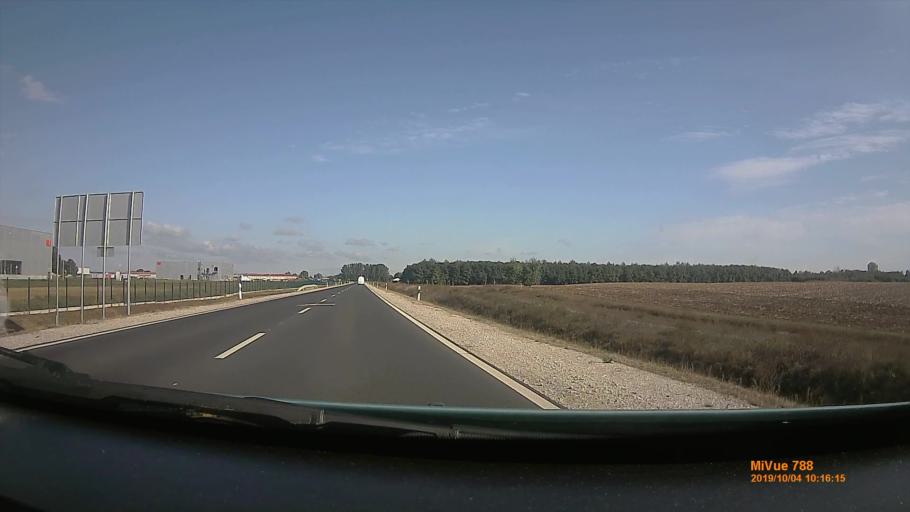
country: HU
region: Szabolcs-Szatmar-Bereg
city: Nyiregyhaza
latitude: 47.9471
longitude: 21.6526
